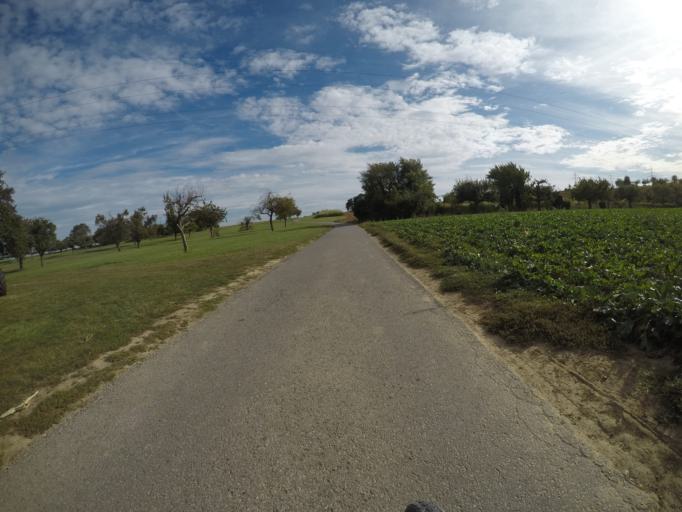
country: DE
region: Baden-Wuerttemberg
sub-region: Regierungsbezirk Stuttgart
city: Leonberg
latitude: 48.8281
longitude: 9.0040
